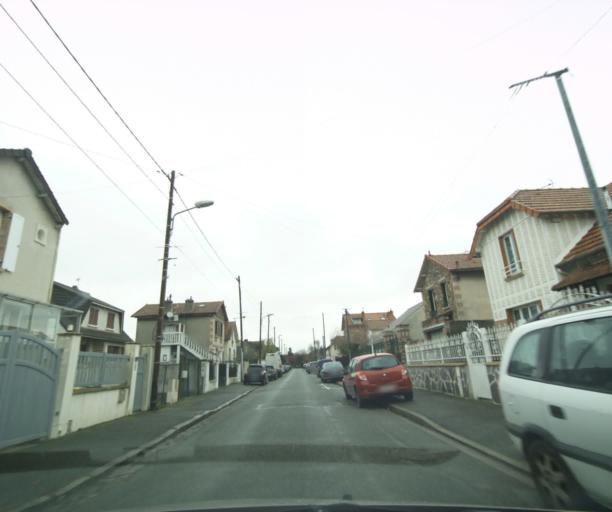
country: FR
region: Ile-de-France
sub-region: Departement du Val-de-Marne
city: Ablon-sur-Seine
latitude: 48.7382
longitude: 2.4191
